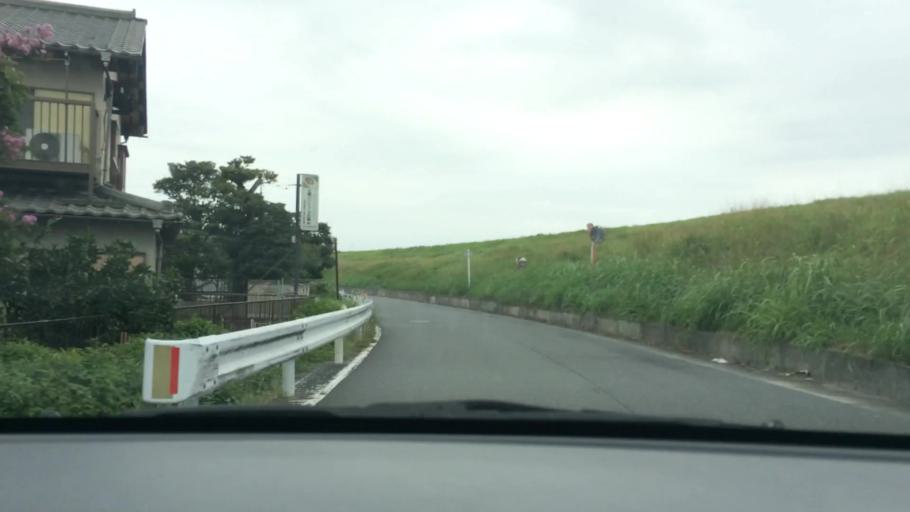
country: JP
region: Chiba
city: Matsudo
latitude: 35.7993
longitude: 139.8889
